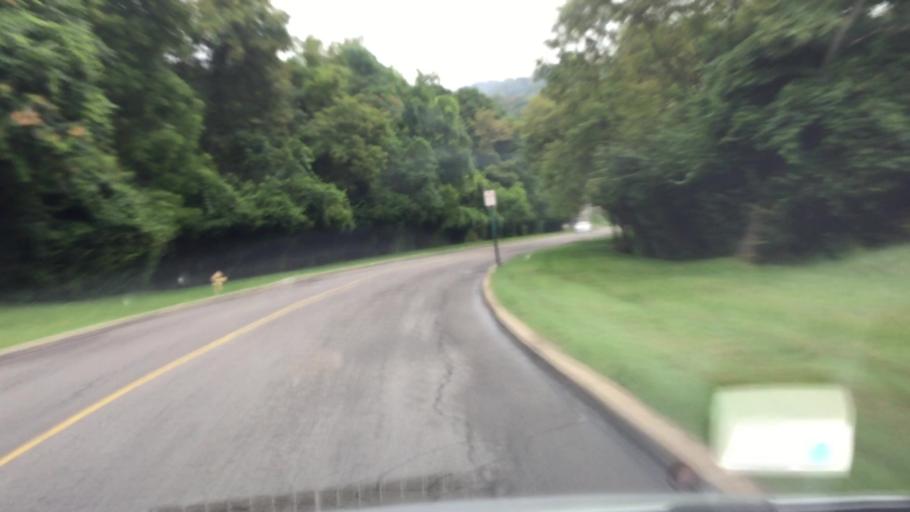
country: US
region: Pennsylvania
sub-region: Allegheny County
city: Crafton
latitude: 40.4237
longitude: -80.0622
